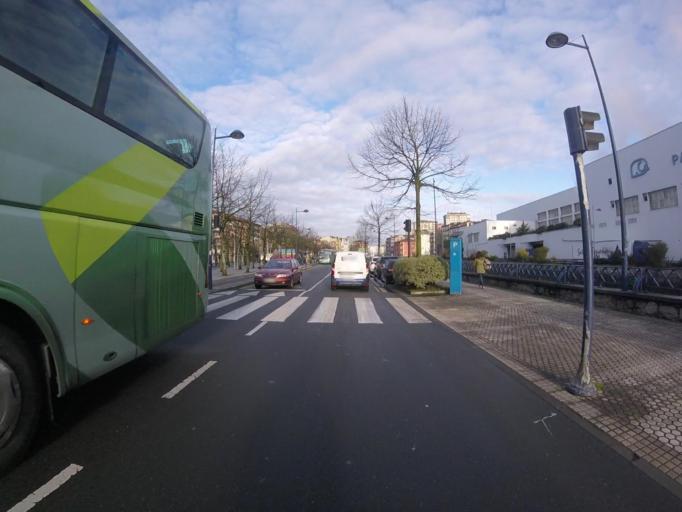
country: ES
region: Basque Country
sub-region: Provincia de Guipuzcoa
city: Errenteria
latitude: 43.3123
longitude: -1.8960
